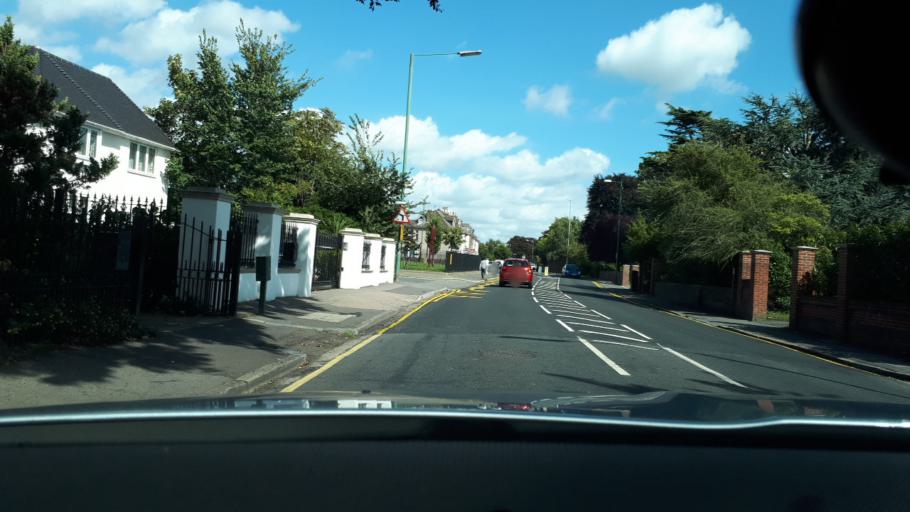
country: GB
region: England
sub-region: Kent
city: Dartford
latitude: 51.4439
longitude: 0.2053
